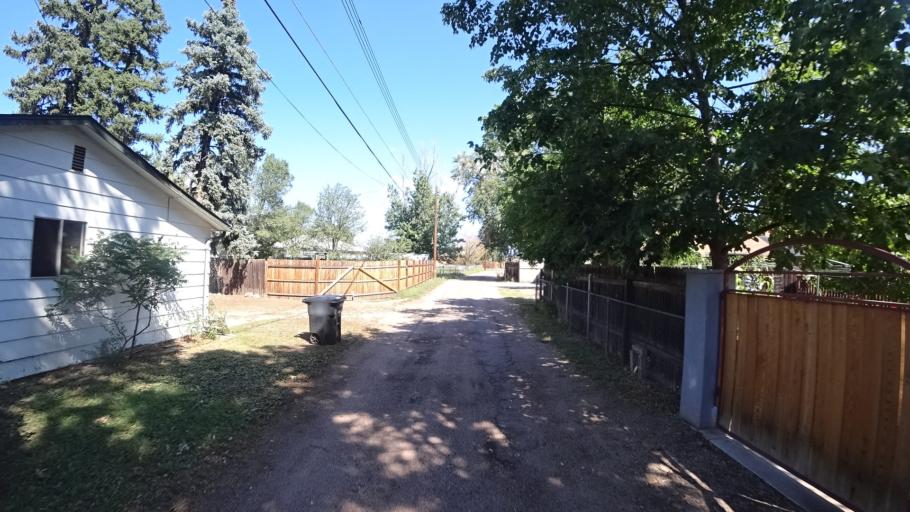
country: US
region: Colorado
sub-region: El Paso County
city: Colorado Springs
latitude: 38.8692
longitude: -104.8163
